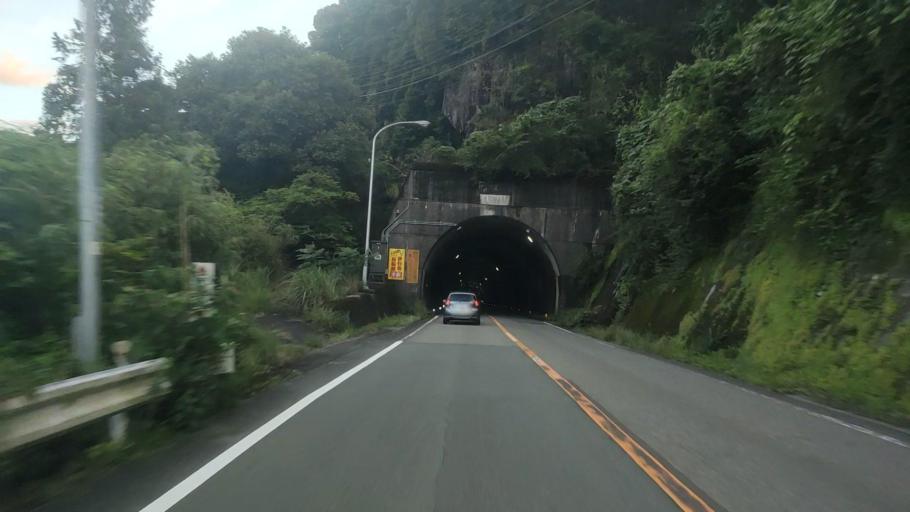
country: JP
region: Wakayama
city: Shingu
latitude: 33.8171
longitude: 135.8563
